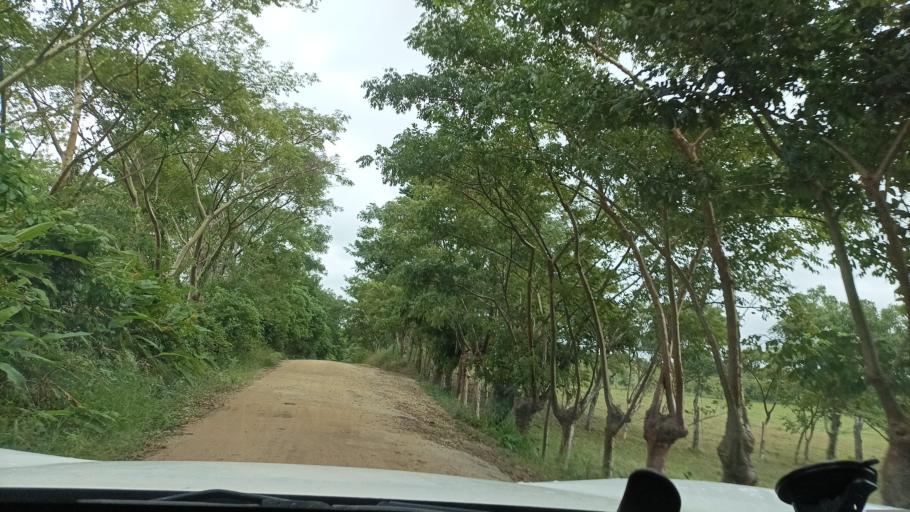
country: MX
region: Veracruz
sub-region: Moloacan
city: Cuichapa
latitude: 17.7906
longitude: -94.3680
